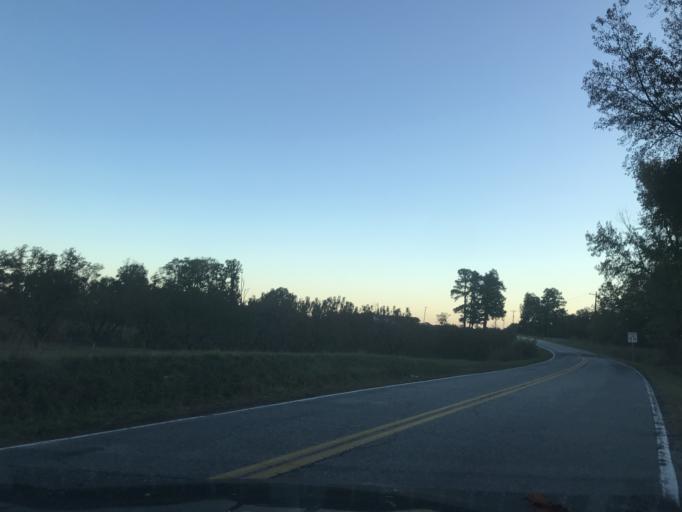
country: US
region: South Carolina
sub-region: Spartanburg County
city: Mayo
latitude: 35.1289
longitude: -81.7754
